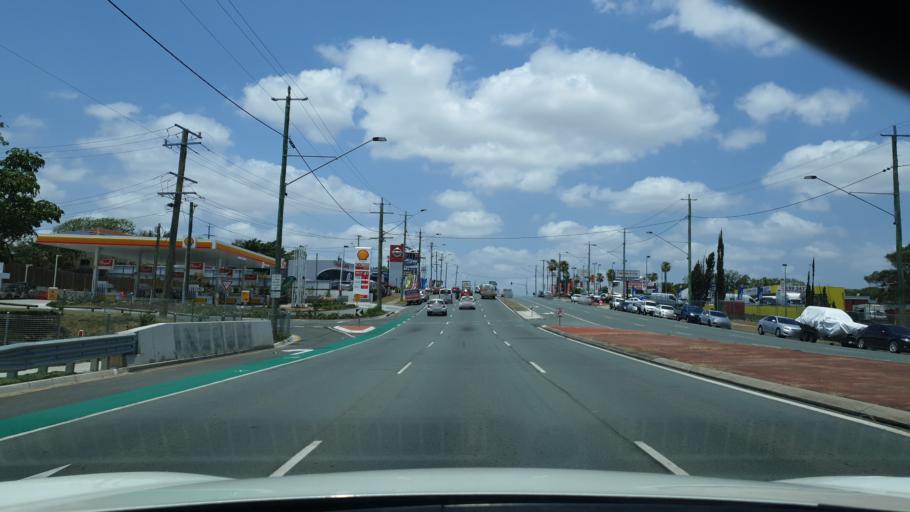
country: AU
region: Queensland
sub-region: Brisbane
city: Wavell Heights
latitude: -27.3971
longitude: 153.0313
